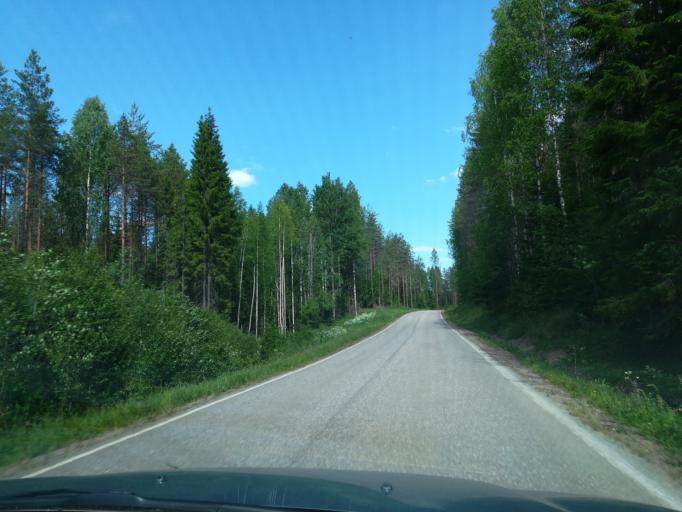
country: FI
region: South Karelia
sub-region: Imatra
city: Ruokolahti
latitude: 61.4746
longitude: 28.7984
